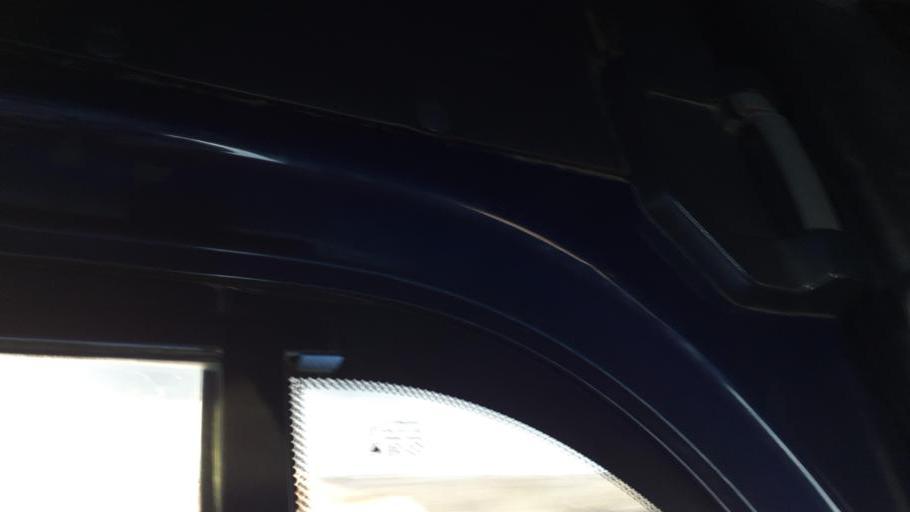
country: BO
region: La Paz
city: Tiahuanaco
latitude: -16.8828
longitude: -68.6812
